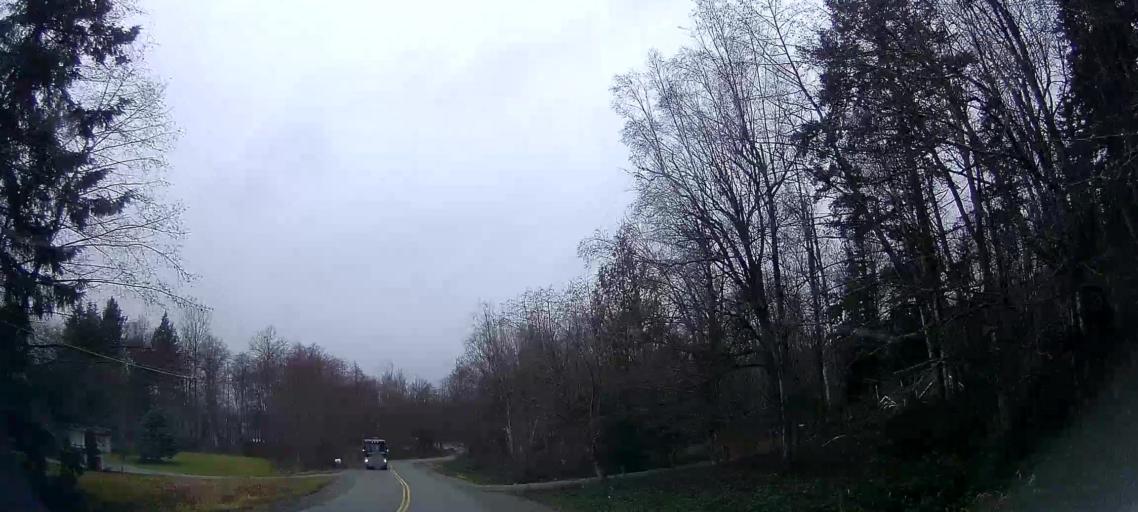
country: US
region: Washington
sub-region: Skagit County
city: Mount Vernon
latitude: 48.3810
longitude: -122.3027
